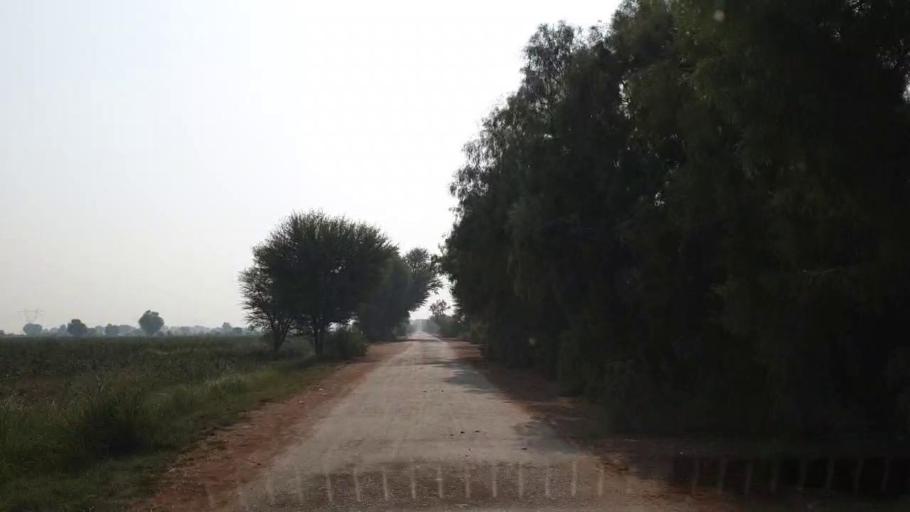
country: PK
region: Sindh
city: Sehwan
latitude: 26.4727
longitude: 67.7745
